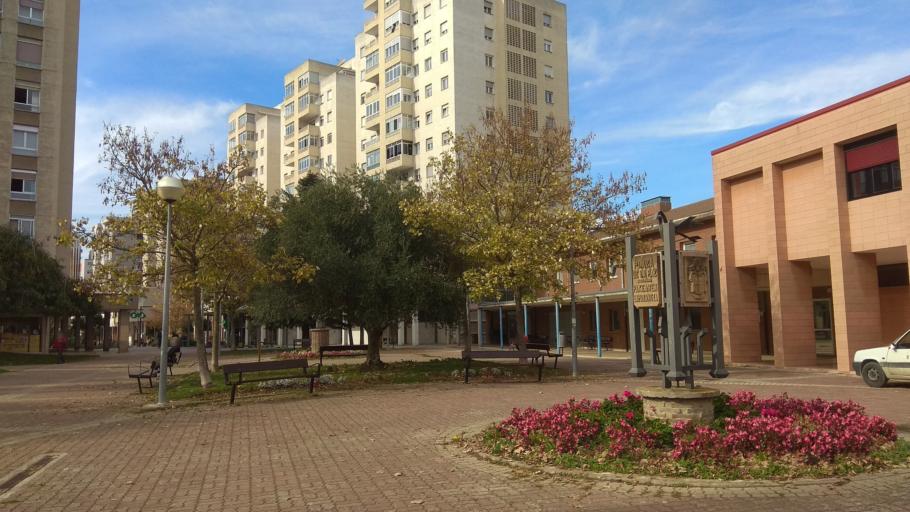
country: ES
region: Navarre
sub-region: Provincia de Navarra
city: Baranain
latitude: 42.8059
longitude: -1.6783
